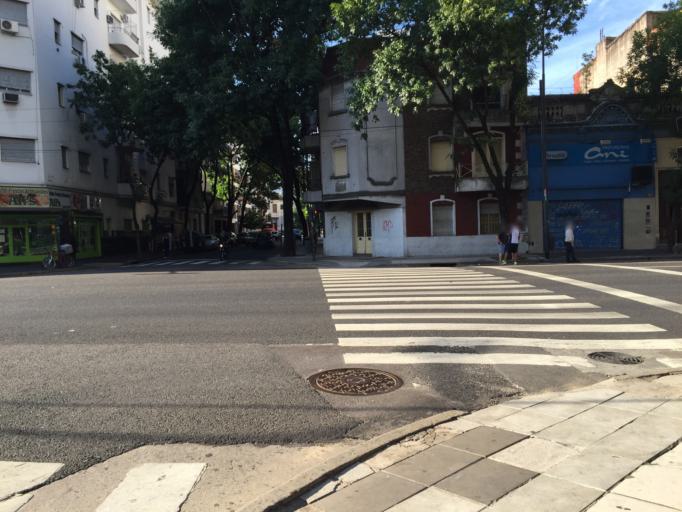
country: AR
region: Buenos Aires F.D.
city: Buenos Aires
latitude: -34.6187
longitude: -58.3990
